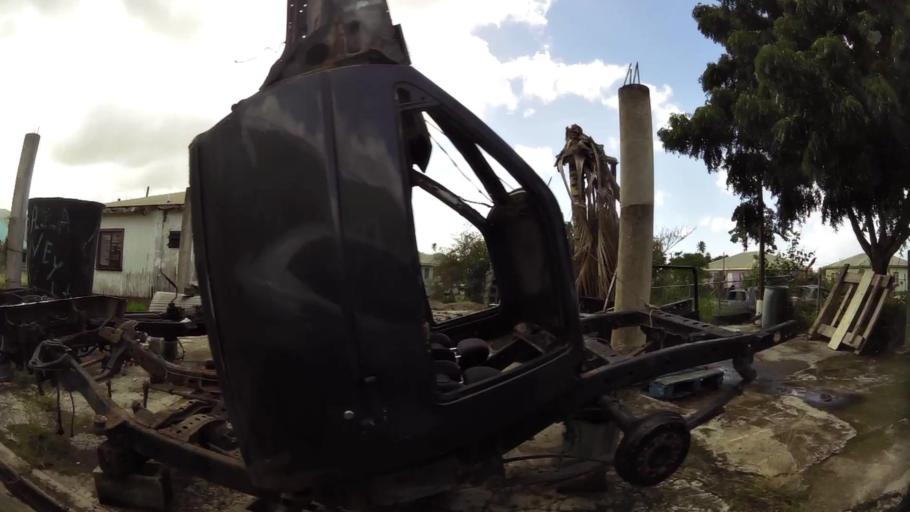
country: AG
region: Saint Mary
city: Bolands
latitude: 17.0772
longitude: -61.8676
